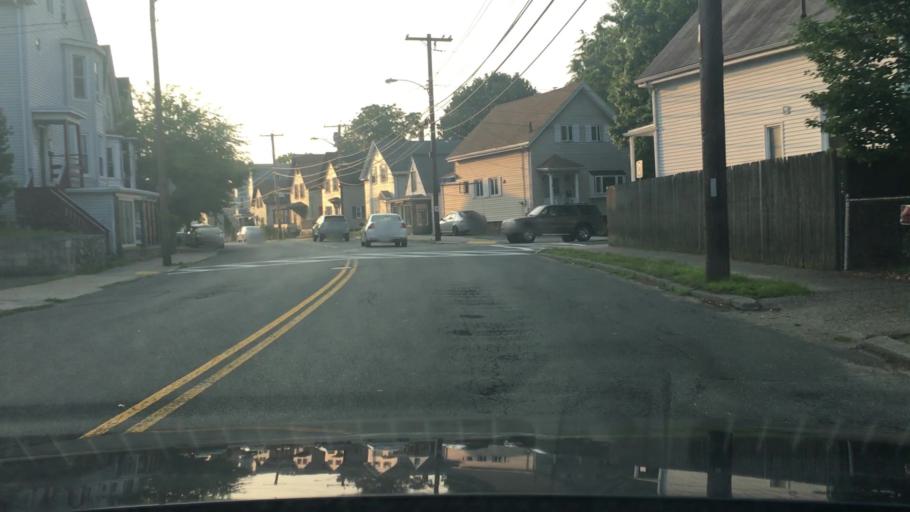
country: US
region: Massachusetts
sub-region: Essex County
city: Lynn
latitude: 42.4692
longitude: -70.9698
